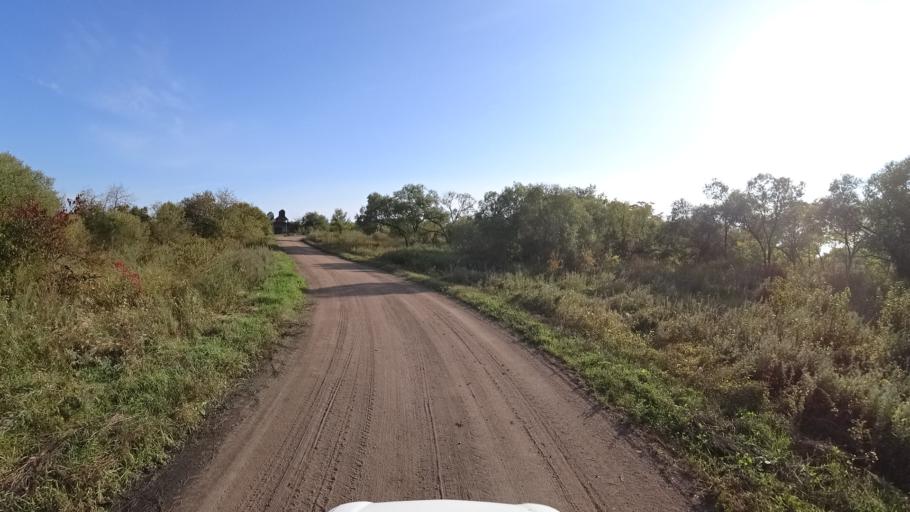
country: RU
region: Amur
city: Arkhara
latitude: 49.3510
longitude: 130.1007
